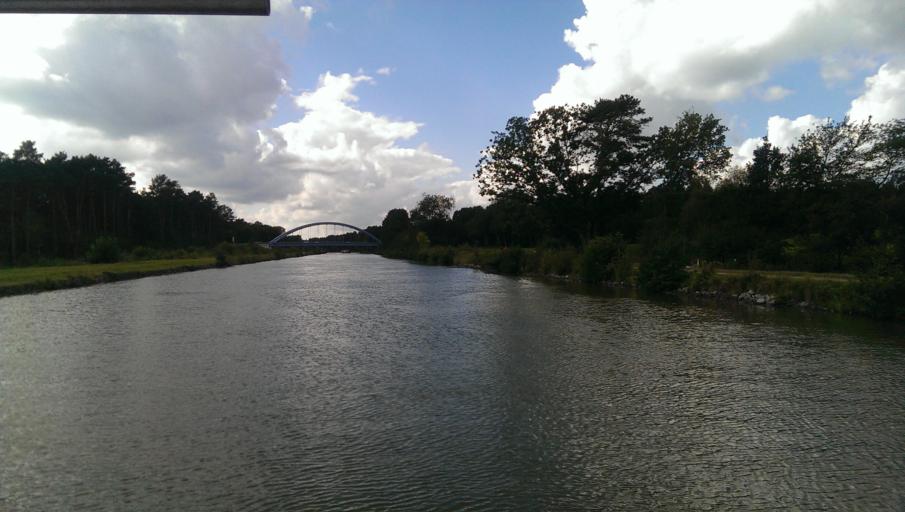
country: DE
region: Brandenburg
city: Marienwerder
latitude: 52.8557
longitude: 13.6574
